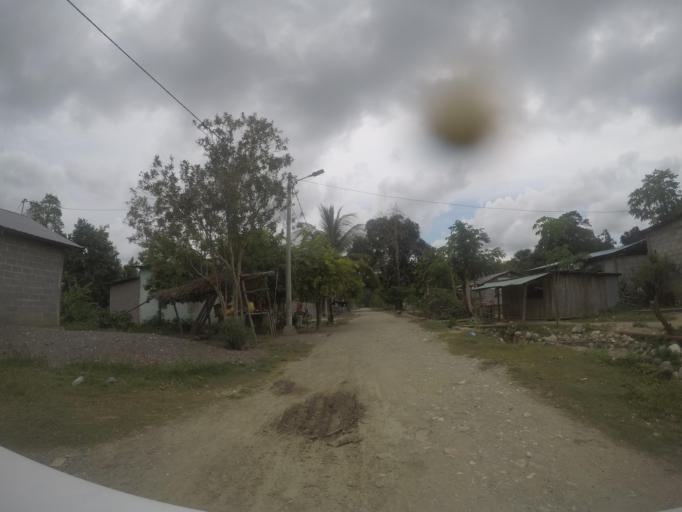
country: TL
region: Viqueque
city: Viqueque
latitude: -8.8786
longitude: 126.3634
